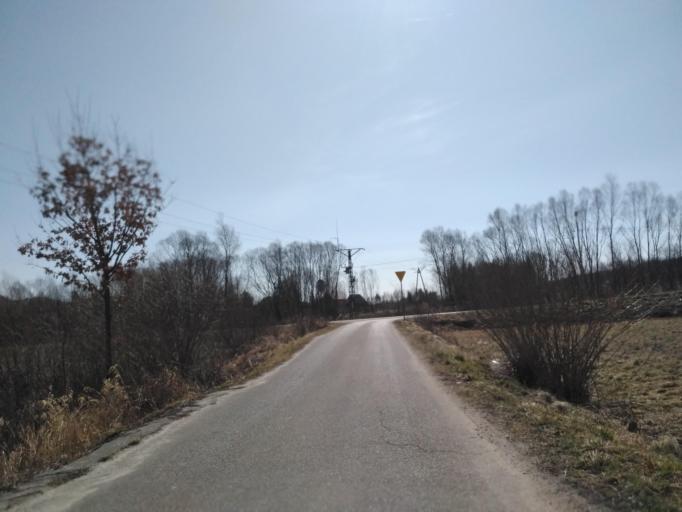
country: PL
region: Subcarpathian Voivodeship
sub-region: Powiat brzozowski
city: Blizne
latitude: 49.7607
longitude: 21.9614
